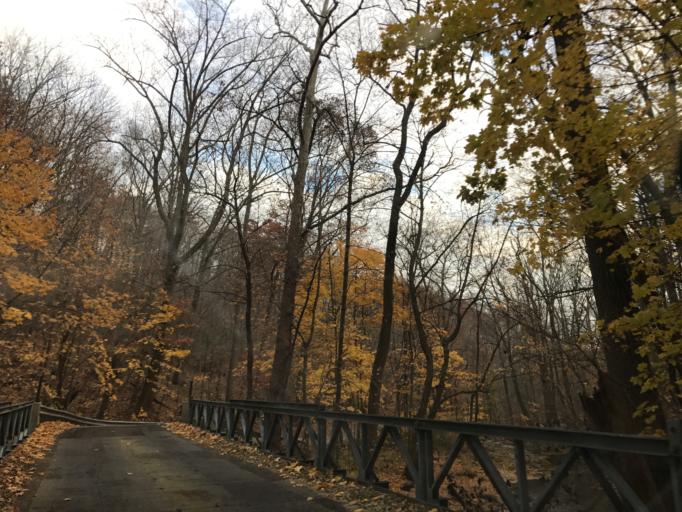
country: US
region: Maryland
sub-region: Baltimore County
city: Perry Hall
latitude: 39.4558
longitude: -76.4797
